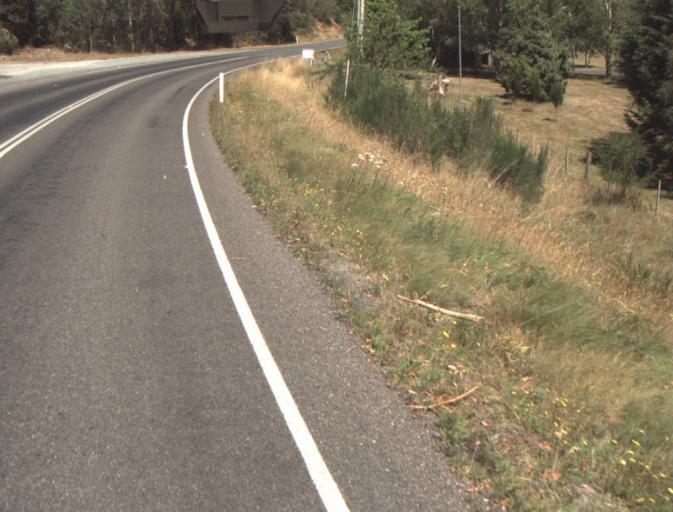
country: AU
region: Tasmania
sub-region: Dorset
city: Scottsdale
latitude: -41.3152
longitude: 147.3674
